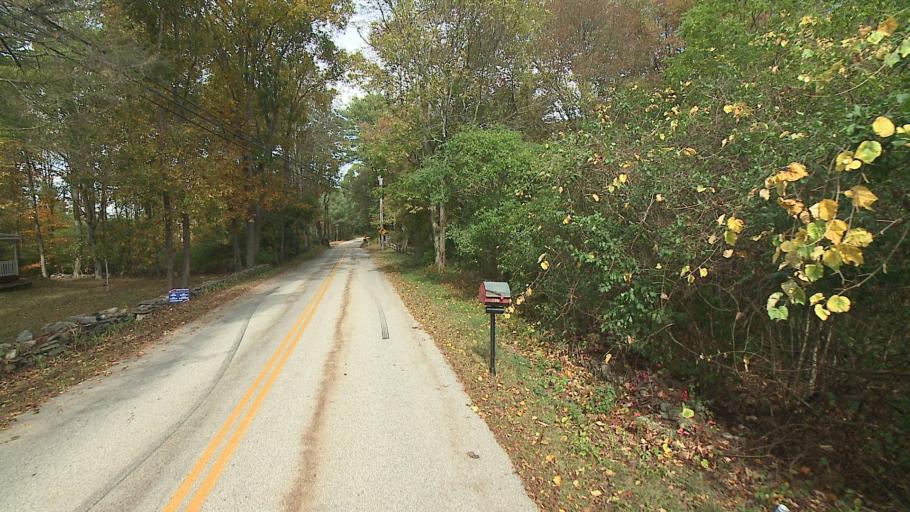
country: US
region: Connecticut
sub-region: Windham County
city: Thompson
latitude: 41.9231
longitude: -71.8212
